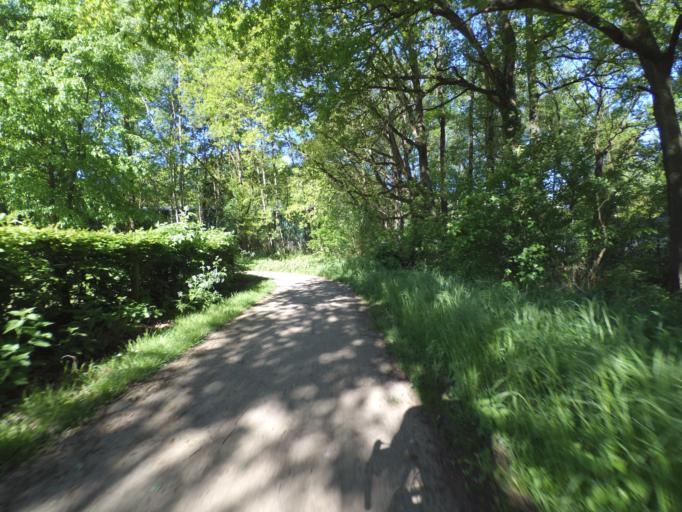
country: NL
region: Gelderland
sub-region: Gemeente Voorst
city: Twello
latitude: 52.1987
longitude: 6.1114
